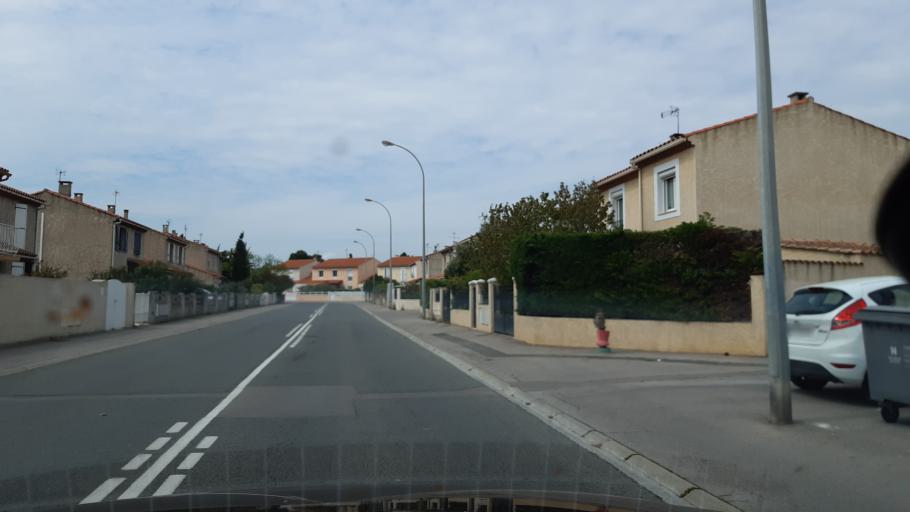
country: FR
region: Languedoc-Roussillon
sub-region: Departement de l'Aude
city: Narbonne
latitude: 43.1889
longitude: 3.0260
